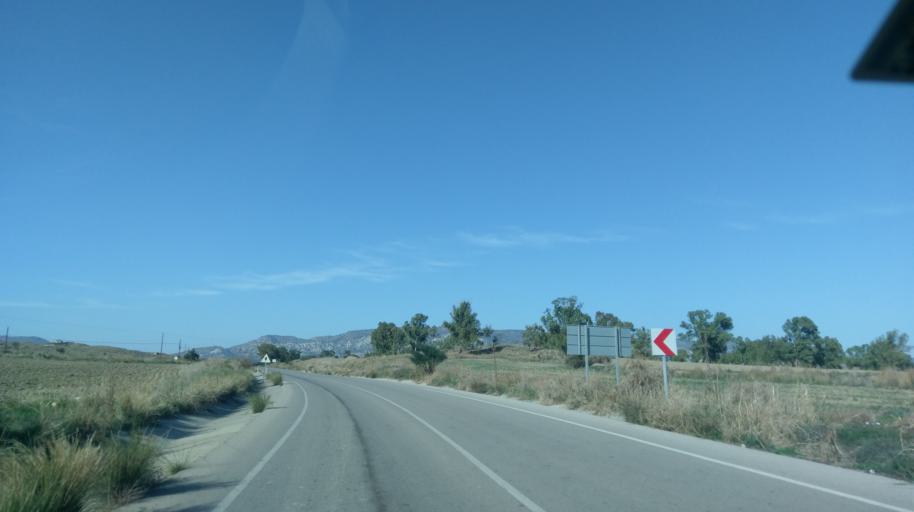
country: CY
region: Ammochostos
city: Lefkonoiko
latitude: 35.2875
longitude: 33.7367
